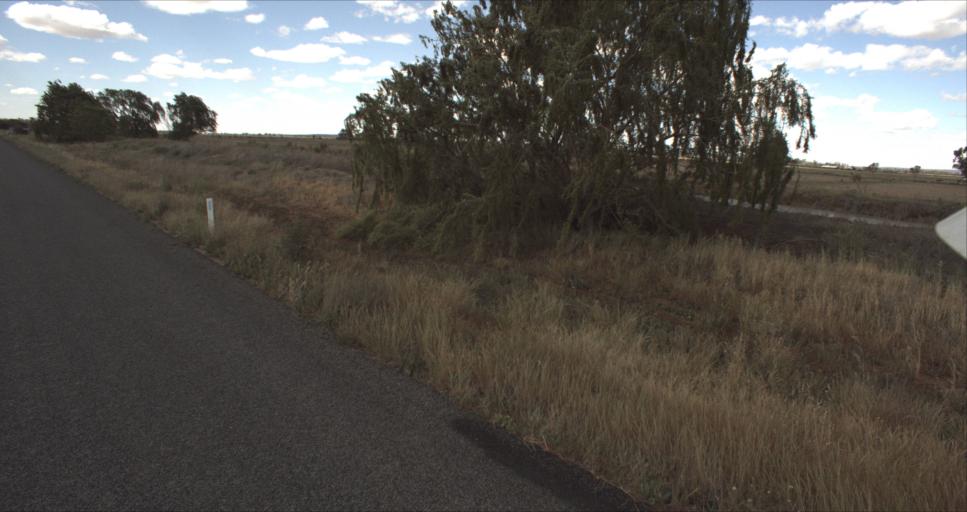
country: AU
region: New South Wales
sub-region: Leeton
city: Leeton
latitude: -34.4457
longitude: 146.2555
